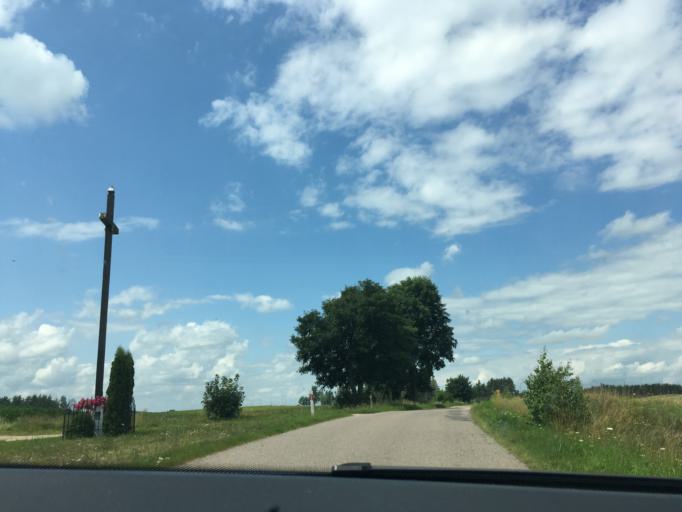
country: PL
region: Podlasie
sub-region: Powiat sejnenski
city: Krasnopol
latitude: 54.0970
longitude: 23.2236
